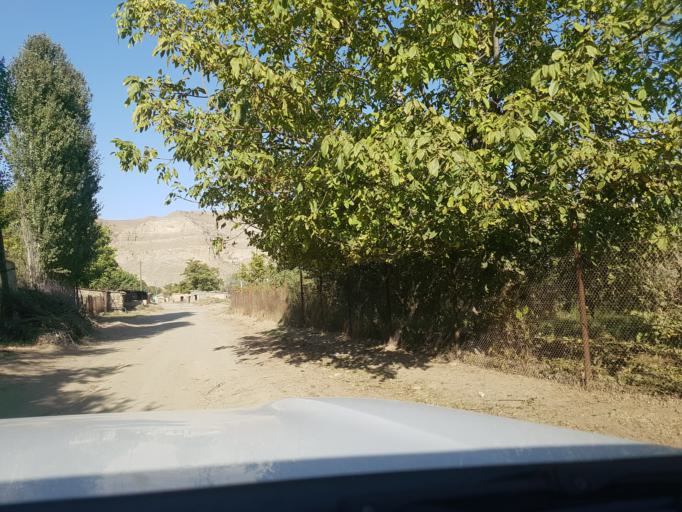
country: TM
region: Balkan
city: Magtymguly
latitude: 38.3008
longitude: 56.7484
